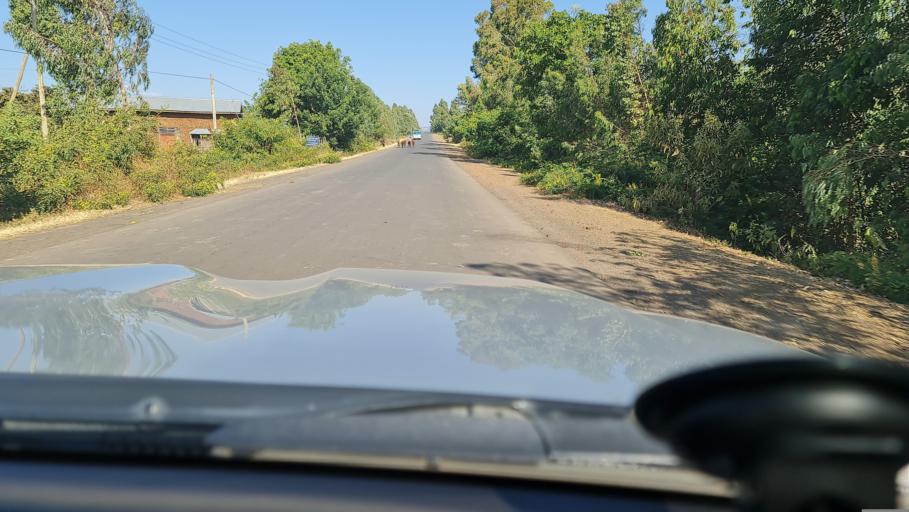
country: ET
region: Oromiya
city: Waliso
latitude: 8.5929
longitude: 37.9344
